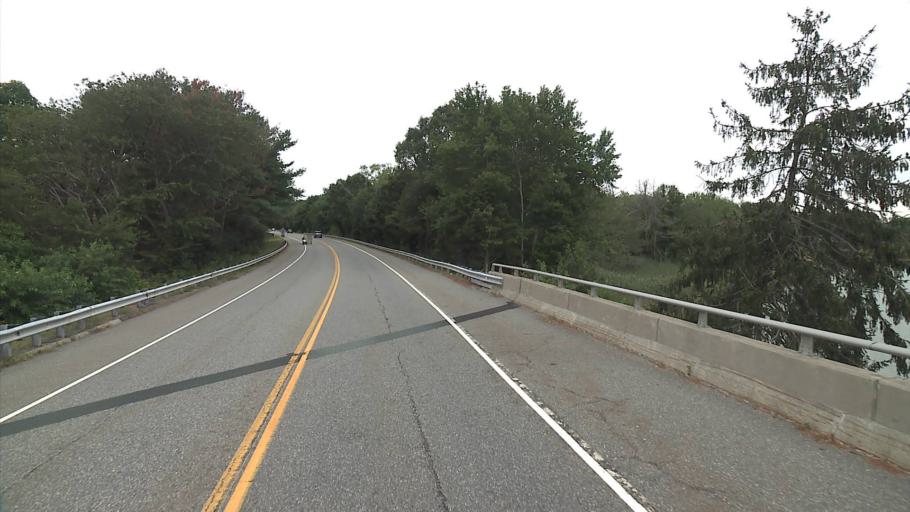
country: US
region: Connecticut
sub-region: Middlesex County
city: Old Saybrook Center
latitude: 41.3065
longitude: -72.3301
